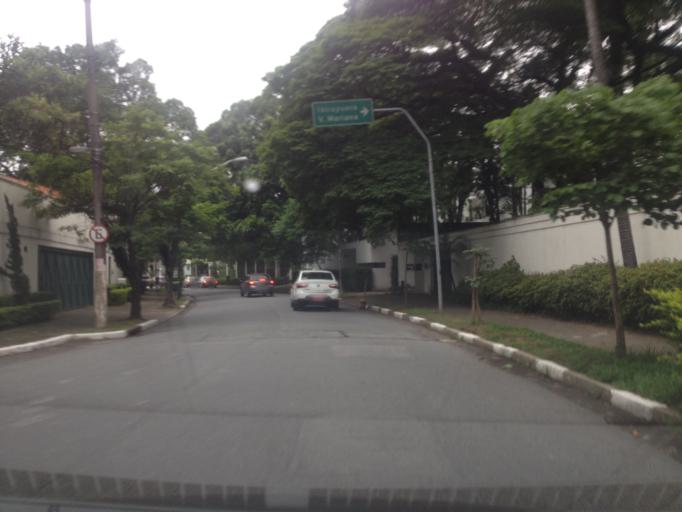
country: BR
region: Sao Paulo
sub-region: Sao Paulo
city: Sao Paulo
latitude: -23.5724
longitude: -46.6703
